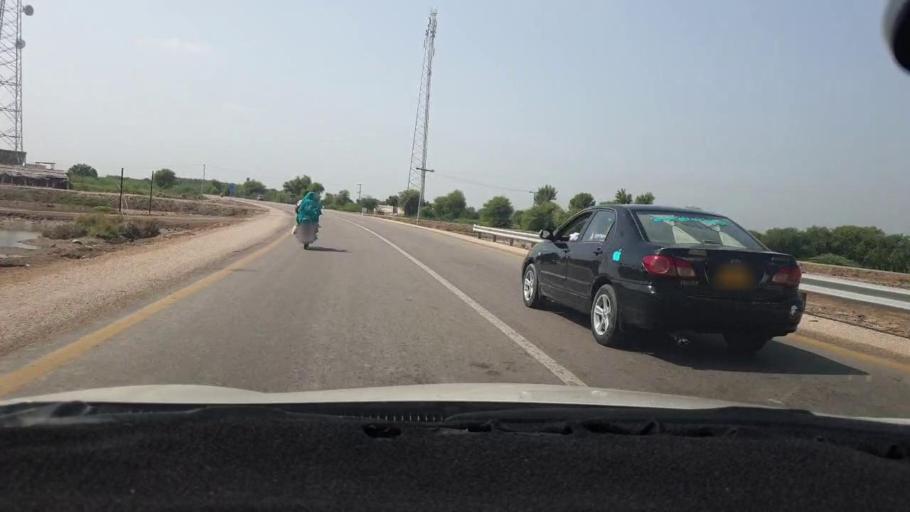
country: PK
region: Sindh
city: Mirpur Khas
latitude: 25.6176
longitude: 69.0835
